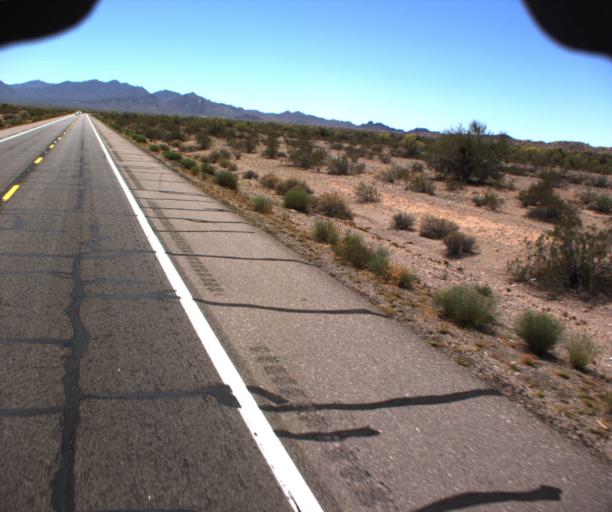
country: US
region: Arizona
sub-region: Mohave County
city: Desert Hills
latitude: 34.7138
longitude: -114.3081
